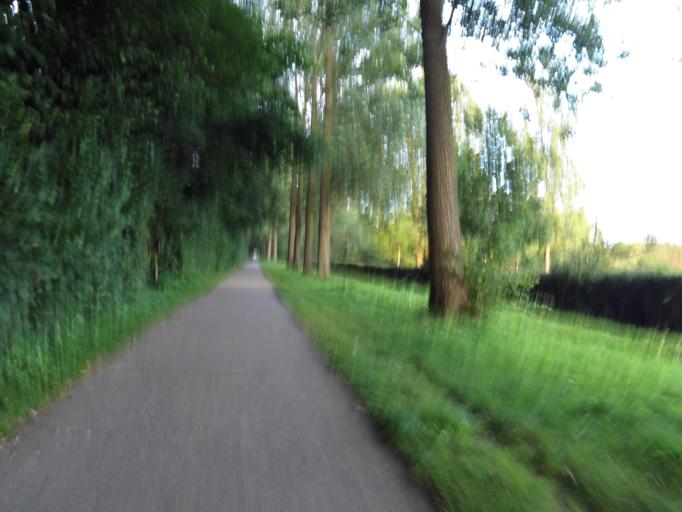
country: BE
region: Flanders
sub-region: Provincie Limburg
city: Tongeren
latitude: 50.7777
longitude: 5.4809
